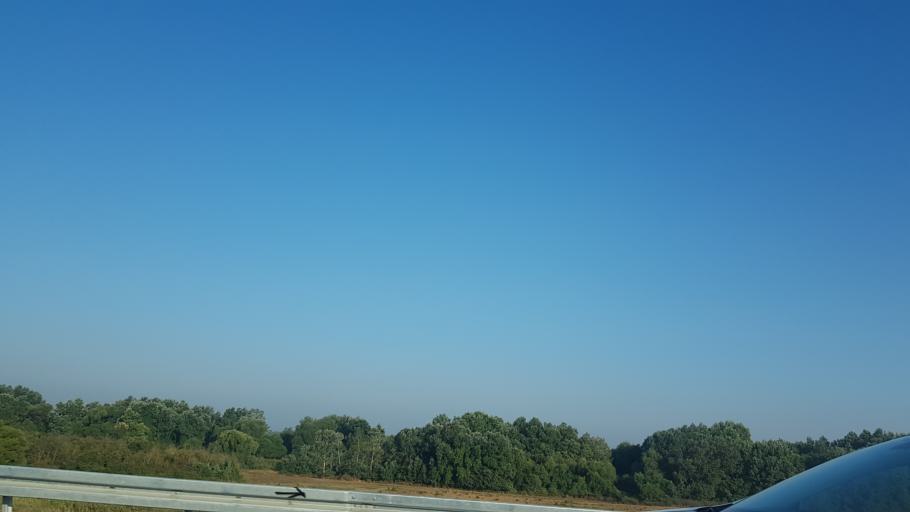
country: TR
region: Bursa
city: Karacabey
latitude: 40.1692
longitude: 28.3214
